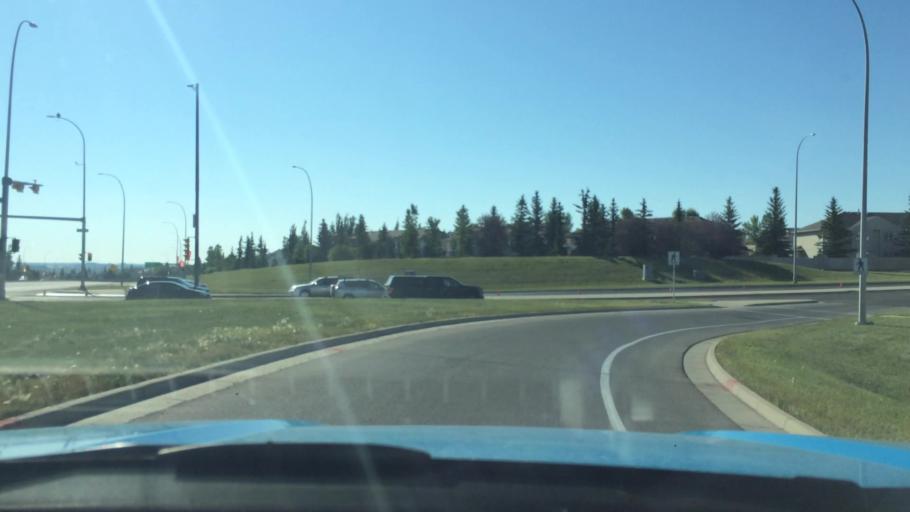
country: CA
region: Alberta
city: Calgary
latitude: 51.1432
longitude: -114.1090
